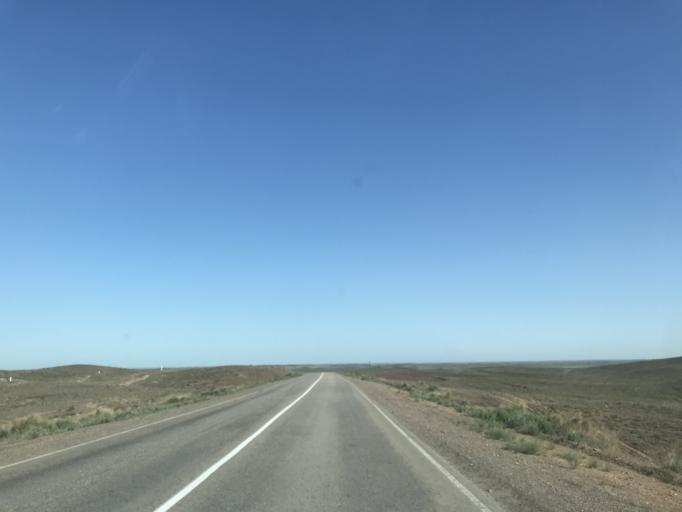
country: KZ
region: Zhambyl
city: Mynaral
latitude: 45.4738
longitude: 73.5527
